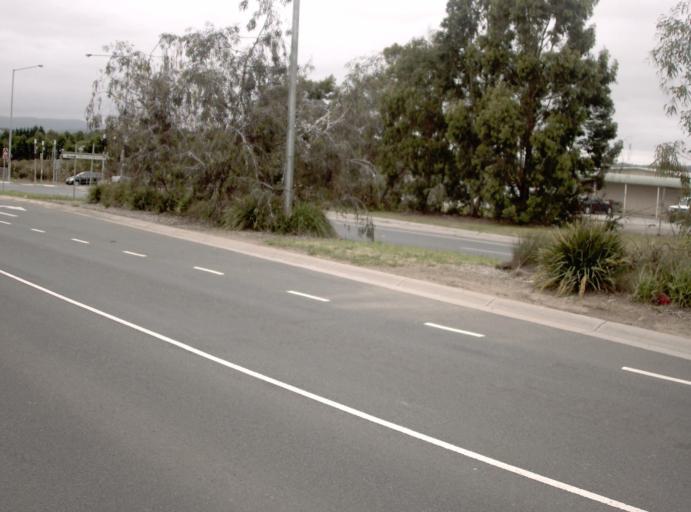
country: AU
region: Victoria
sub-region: Casey
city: Hallam
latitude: -37.9990
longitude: 145.2748
